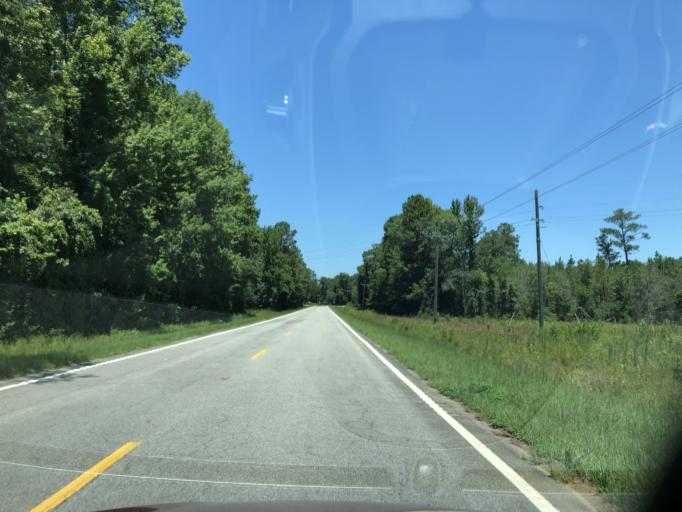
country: US
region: South Carolina
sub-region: Orangeburg County
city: Branchville
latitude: 33.2267
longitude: -80.8859
